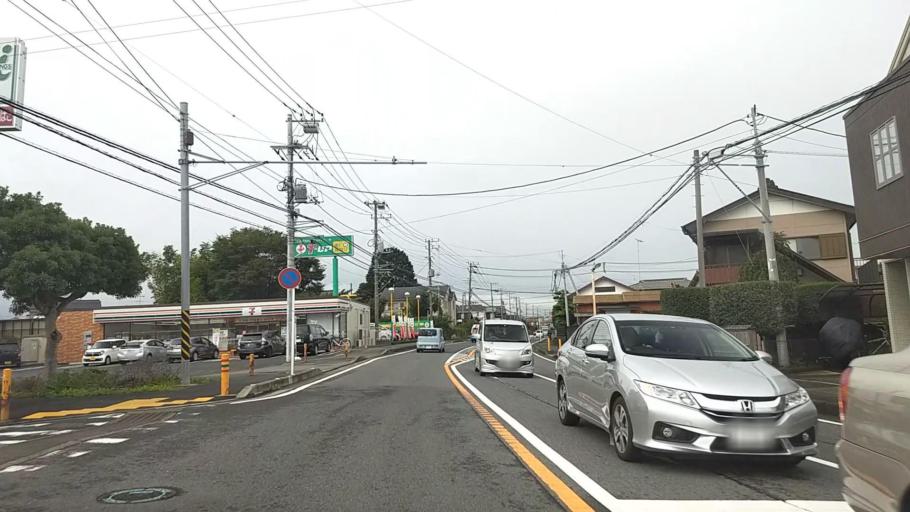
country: JP
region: Kanagawa
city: Atsugi
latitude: 35.4365
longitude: 139.3520
